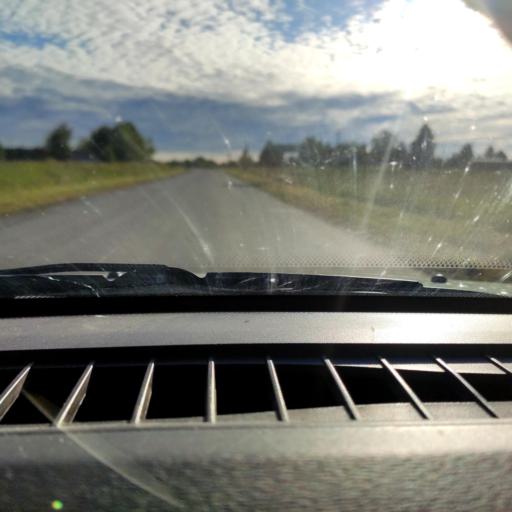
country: RU
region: Perm
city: Uinskoye
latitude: 57.0927
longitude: 56.6371
